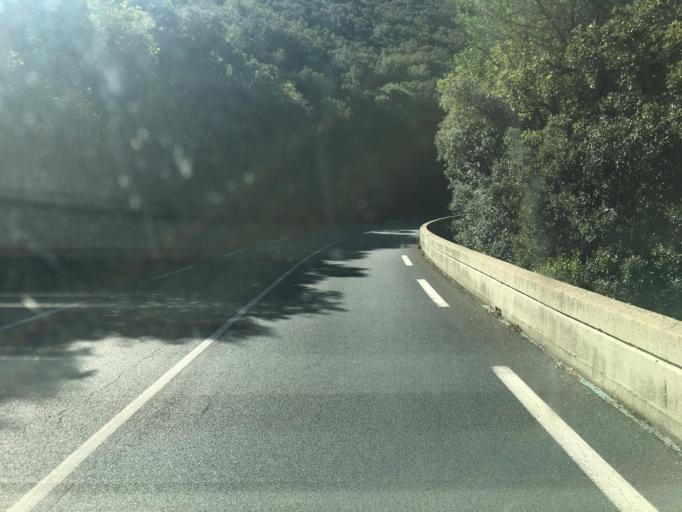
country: FR
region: Languedoc-Roussillon
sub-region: Departement de l'Herault
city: Nebian
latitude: 43.6097
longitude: 3.3876
